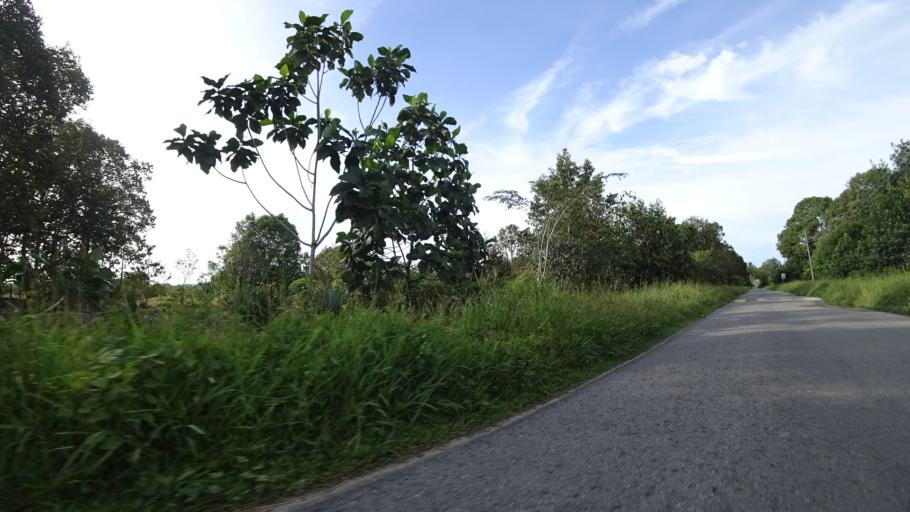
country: BN
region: Brunei and Muara
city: Bandar Seri Begawan
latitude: 4.8109
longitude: 114.8275
